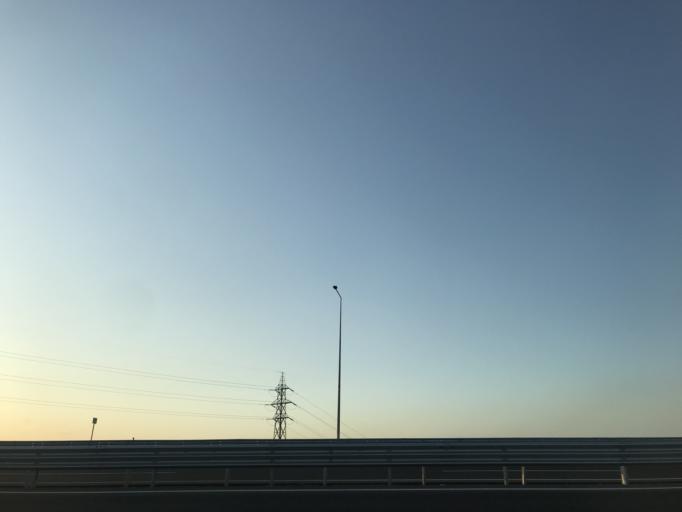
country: TR
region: Kocaeli
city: Tavsanli
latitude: 40.8008
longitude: 29.5184
